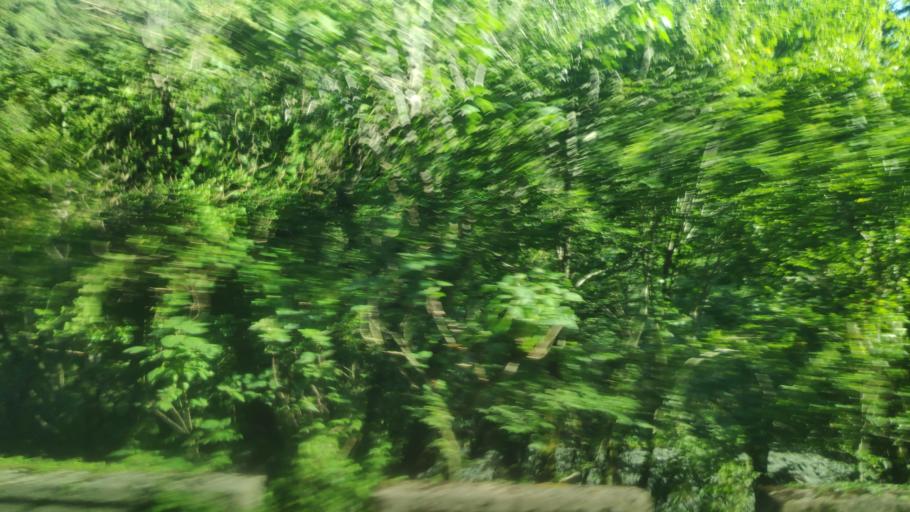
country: GE
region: Abkhazia
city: Gagra
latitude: 43.3528
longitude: 40.4171
